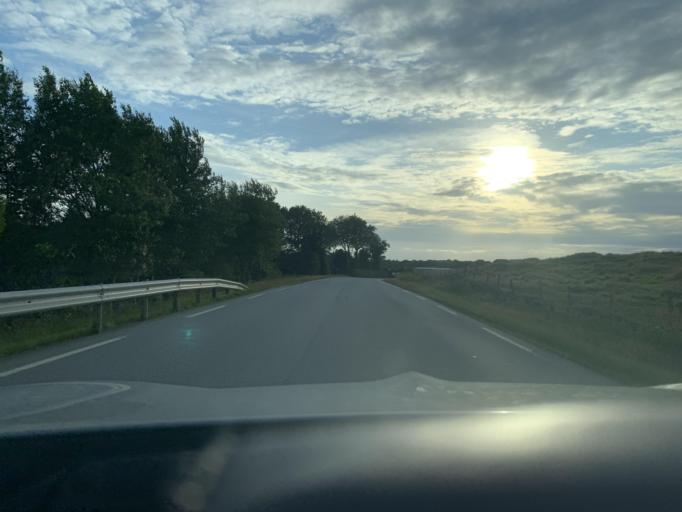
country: NO
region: Rogaland
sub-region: Ha
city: Naerbo
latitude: 58.6850
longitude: 5.7361
